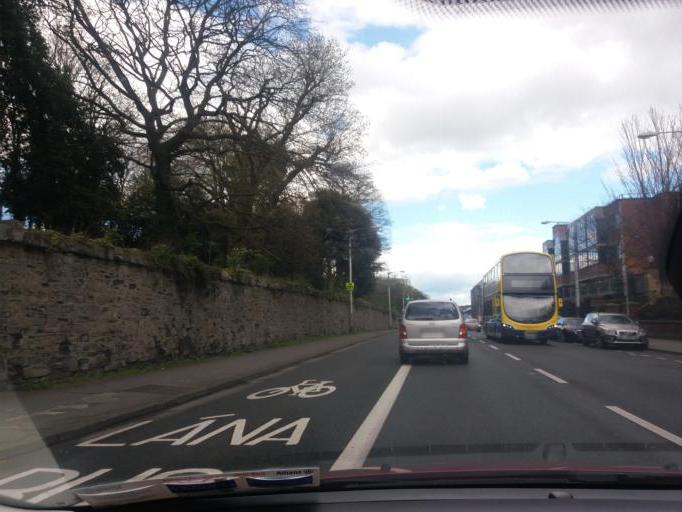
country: IE
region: Leinster
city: Rialto
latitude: 53.3483
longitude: -6.3028
